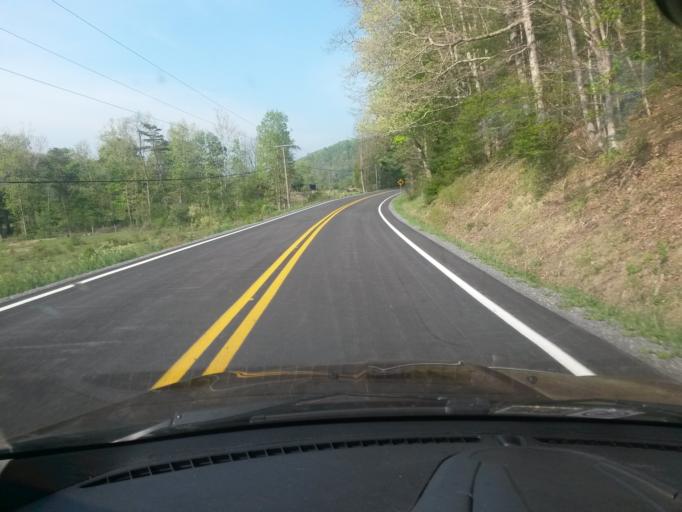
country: US
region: West Virginia
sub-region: Pocahontas County
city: Marlinton
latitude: 38.0076
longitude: -80.0617
